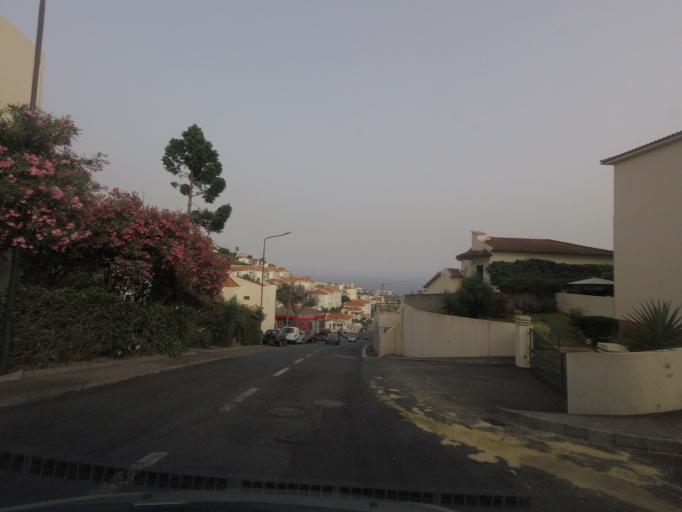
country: PT
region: Madeira
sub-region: Funchal
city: Nossa Senhora do Monte
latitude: 32.6637
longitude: -16.9296
